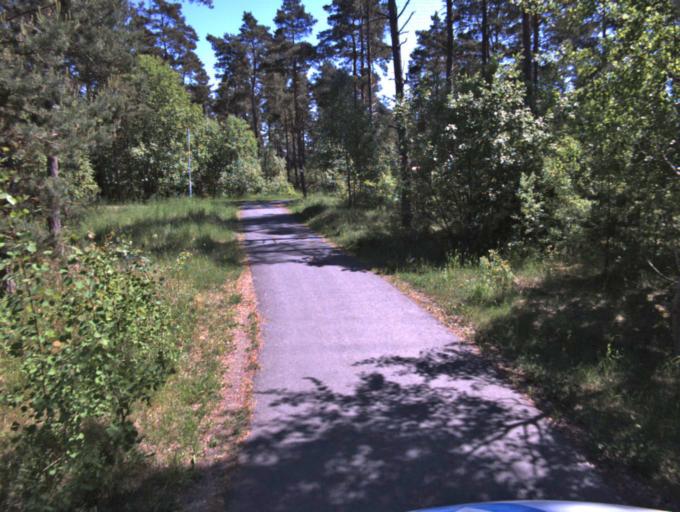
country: SE
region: Skane
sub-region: Kristianstads Kommun
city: Ahus
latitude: 55.9425
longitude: 14.2906
